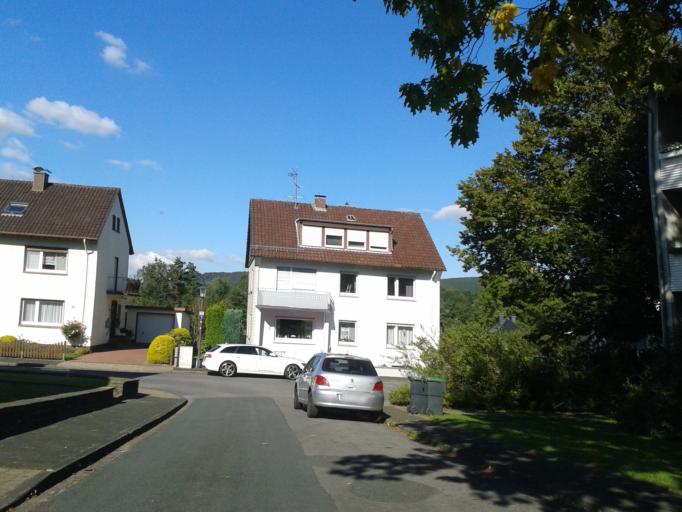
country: DE
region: North Rhine-Westphalia
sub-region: Regierungsbezirk Detmold
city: Lemgo
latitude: 52.0190
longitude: 8.9221
